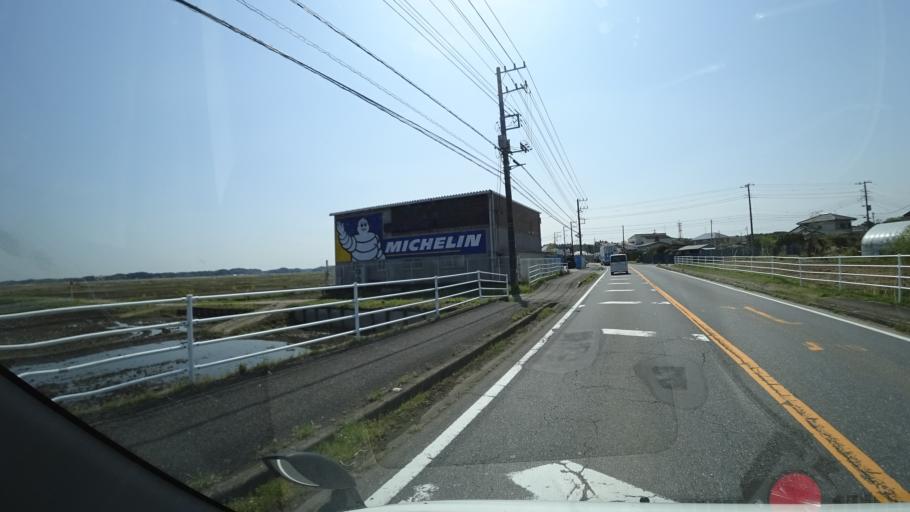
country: JP
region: Chiba
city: Narita
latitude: 35.8458
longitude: 140.2966
